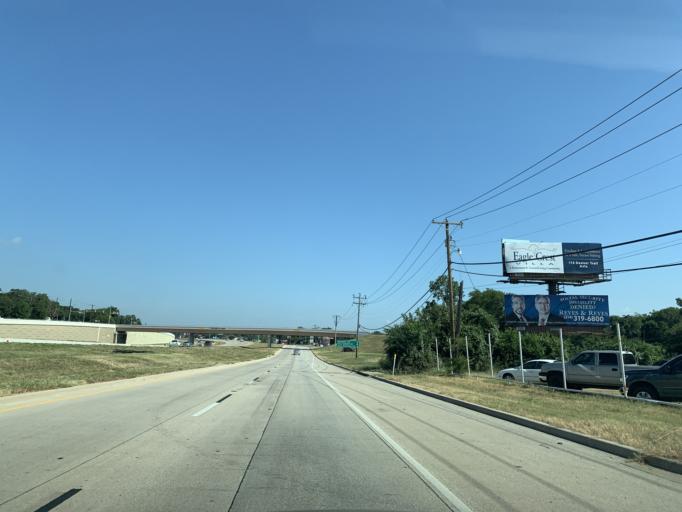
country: US
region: Texas
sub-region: Tarrant County
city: Azle
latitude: 32.8648
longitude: -97.5227
